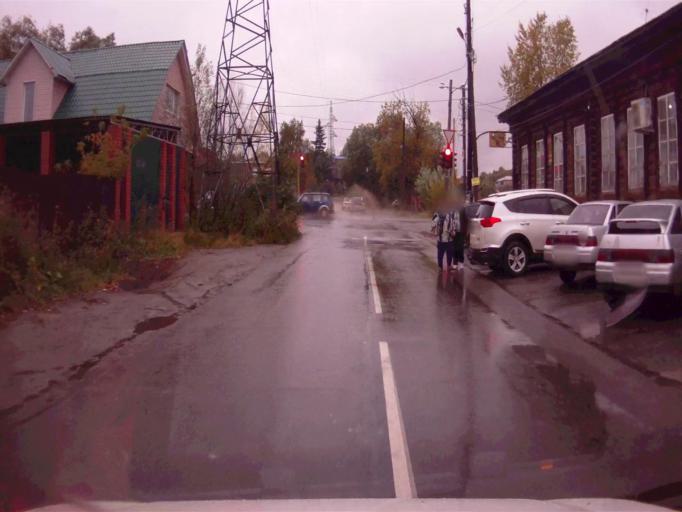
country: RU
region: Chelyabinsk
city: Kyshtym
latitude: 55.7157
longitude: 60.5421
